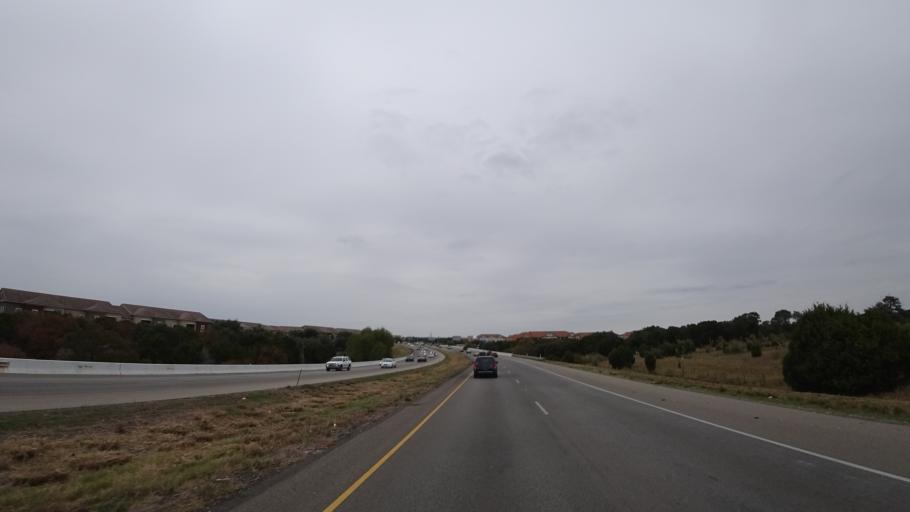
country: US
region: Texas
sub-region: Williamson County
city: Brushy Creek
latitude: 30.5281
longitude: -97.7774
